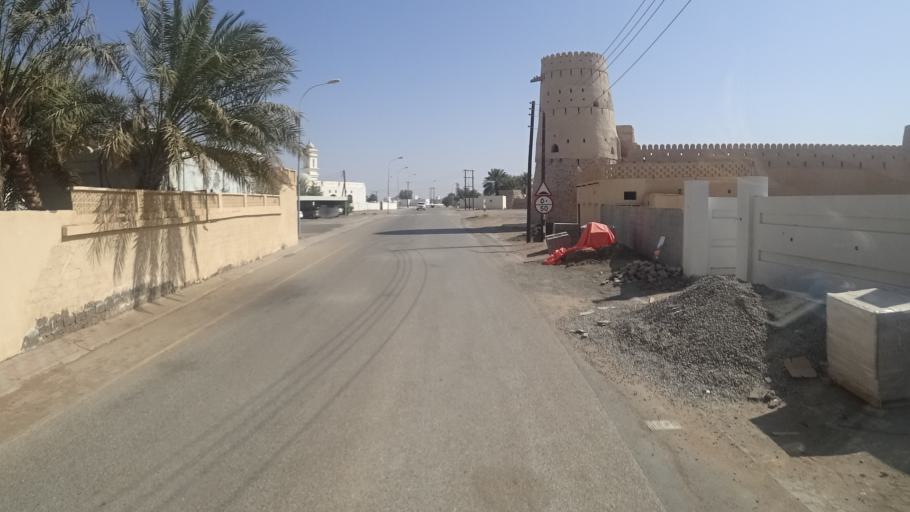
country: OM
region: Ash Sharqiyah
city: Badiyah
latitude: 22.5013
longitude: 58.7427
